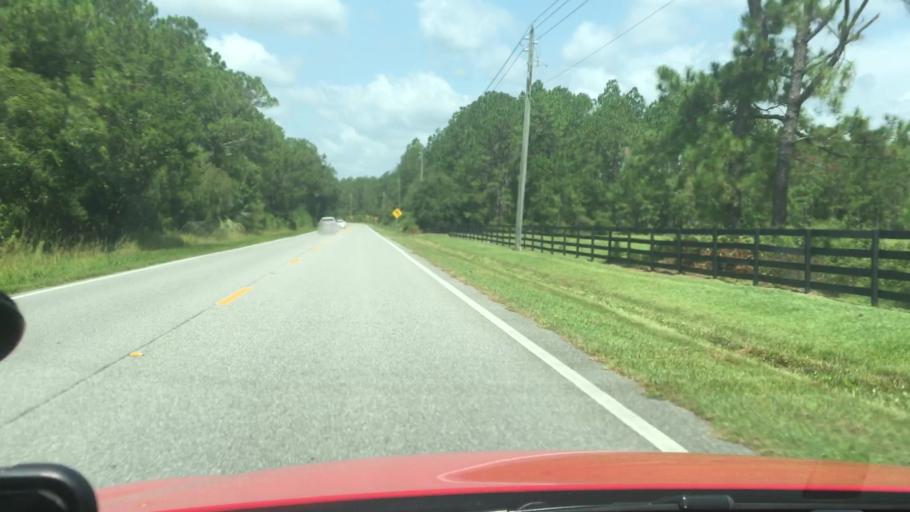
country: US
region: Florida
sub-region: Volusia County
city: Samsula-Spruce Creek
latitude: 29.0266
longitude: -81.1074
